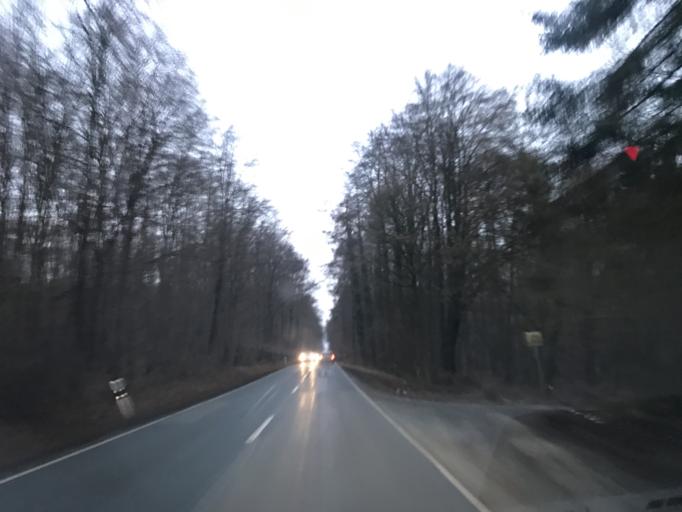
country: DE
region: Hesse
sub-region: Regierungsbezirk Kassel
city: Calden
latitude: 51.3855
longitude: 9.4173
